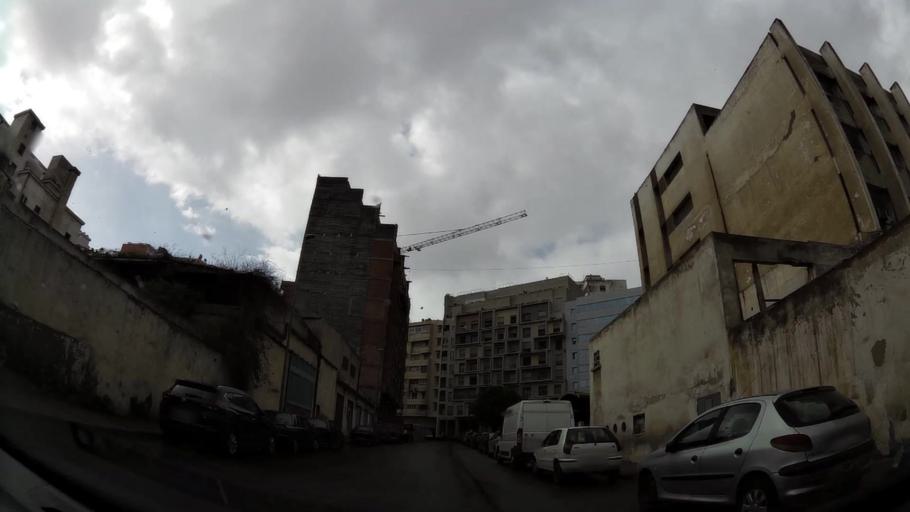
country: MA
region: Grand Casablanca
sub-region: Casablanca
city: Casablanca
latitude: 33.5946
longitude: -7.5989
